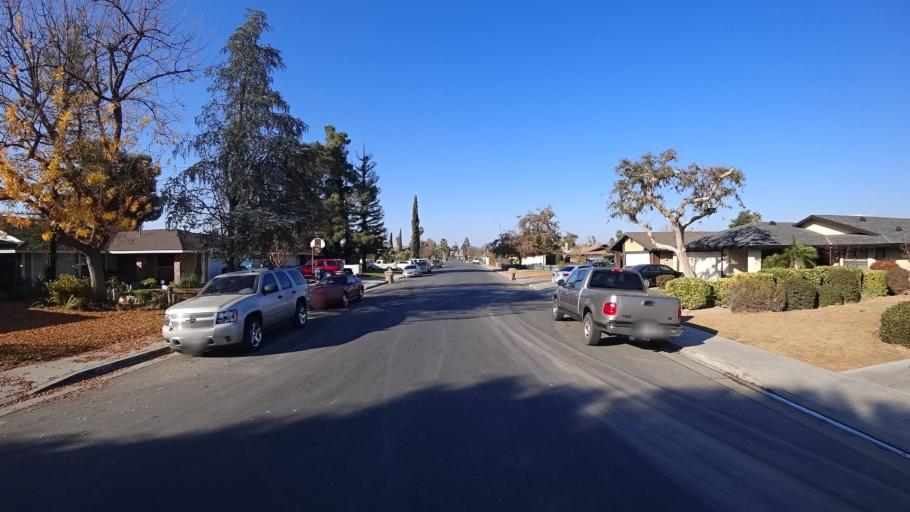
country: US
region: California
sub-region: Kern County
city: Greenfield
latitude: 35.3072
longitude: -119.0177
